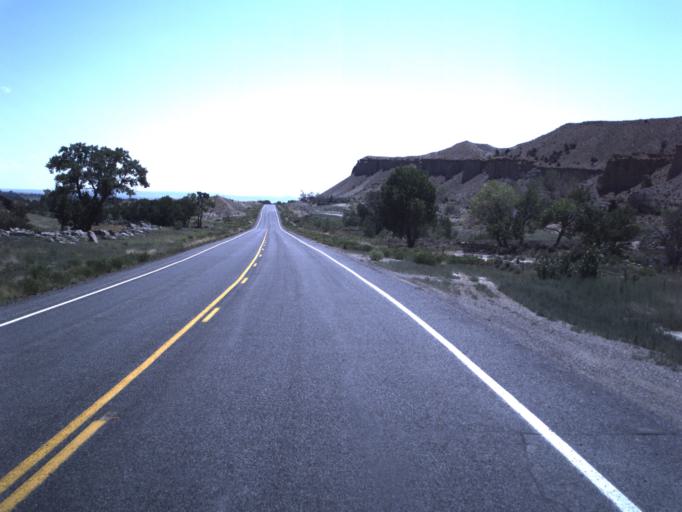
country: US
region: Utah
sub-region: Emery County
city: Orangeville
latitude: 39.2357
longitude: -111.0861
